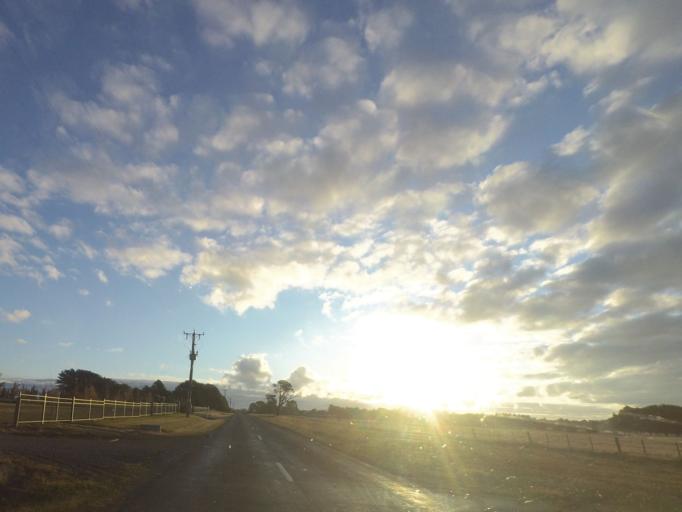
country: AU
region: Victoria
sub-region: Hume
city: Sunbury
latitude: -37.2863
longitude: 144.5106
